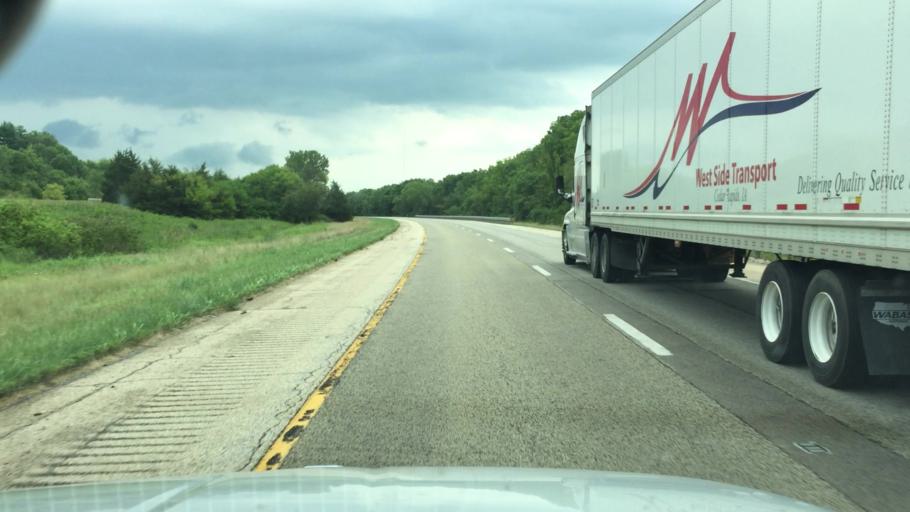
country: US
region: Illinois
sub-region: Peoria County
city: Hanna City
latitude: 40.7925
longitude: -89.7994
